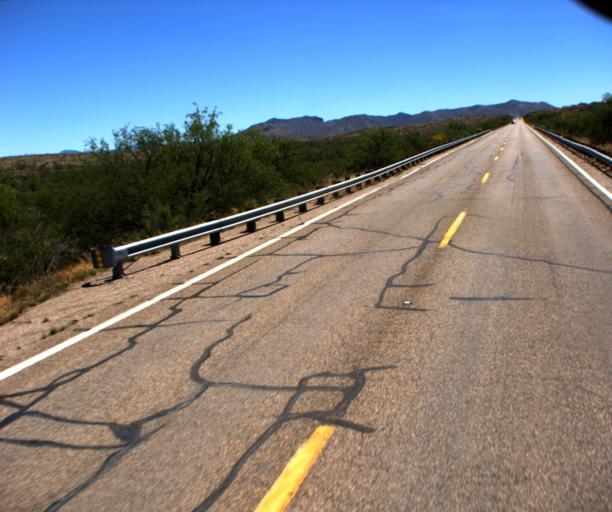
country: US
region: Arizona
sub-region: Pima County
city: Vail
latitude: 31.9821
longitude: -110.6798
